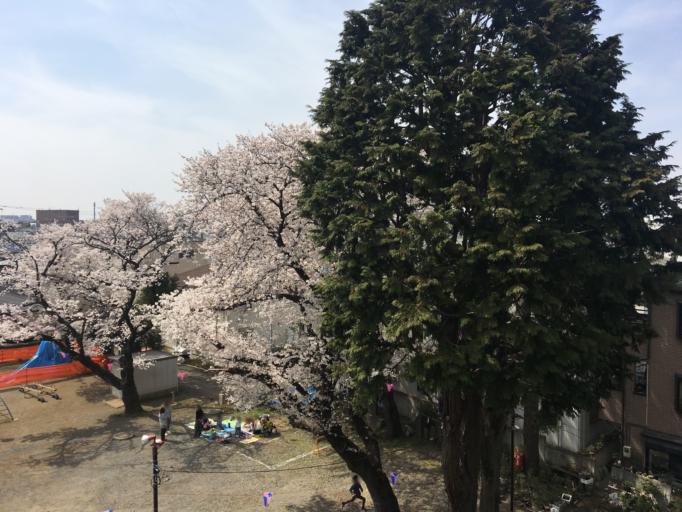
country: JP
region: Saitama
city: Shiki
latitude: 35.8334
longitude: 139.5819
